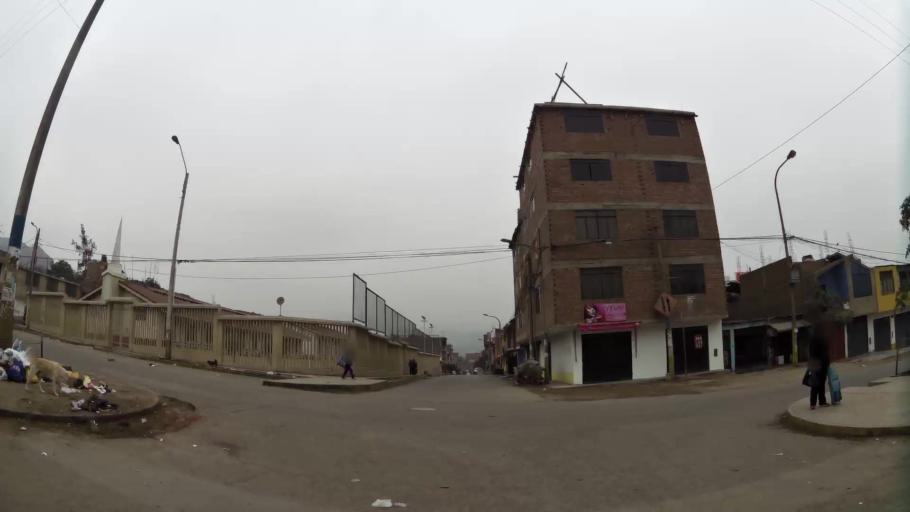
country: PE
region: Lima
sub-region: Lima
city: Independencia
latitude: -11.9403
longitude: -76.9908
